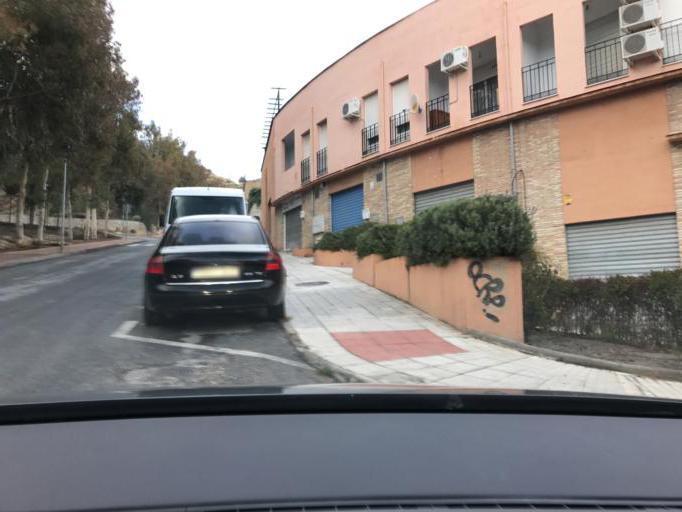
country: ES
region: Andalusia
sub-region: Provincia de Granada
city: Cenes de la Vega
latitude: 37.1639
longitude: -3.5445
